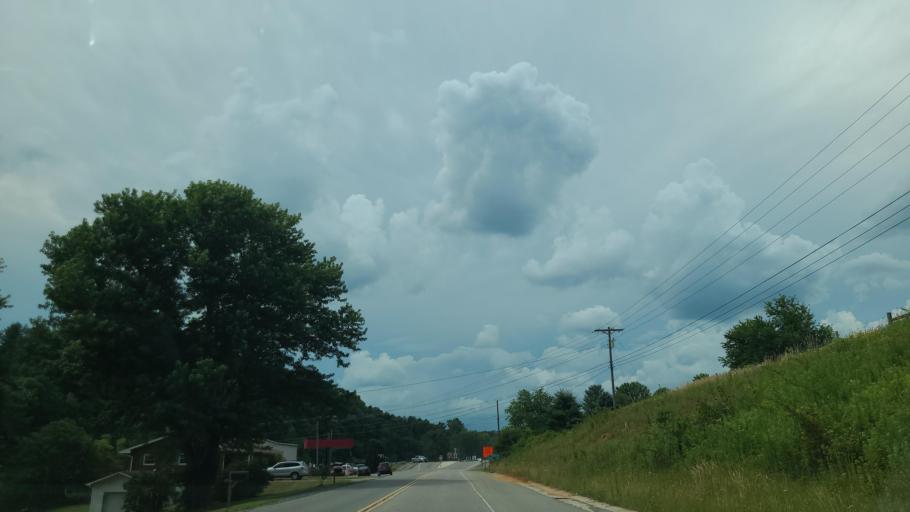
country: US
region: North Carolina
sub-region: Ashe County
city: Jefferson
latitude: 36.3933
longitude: -81.4061
